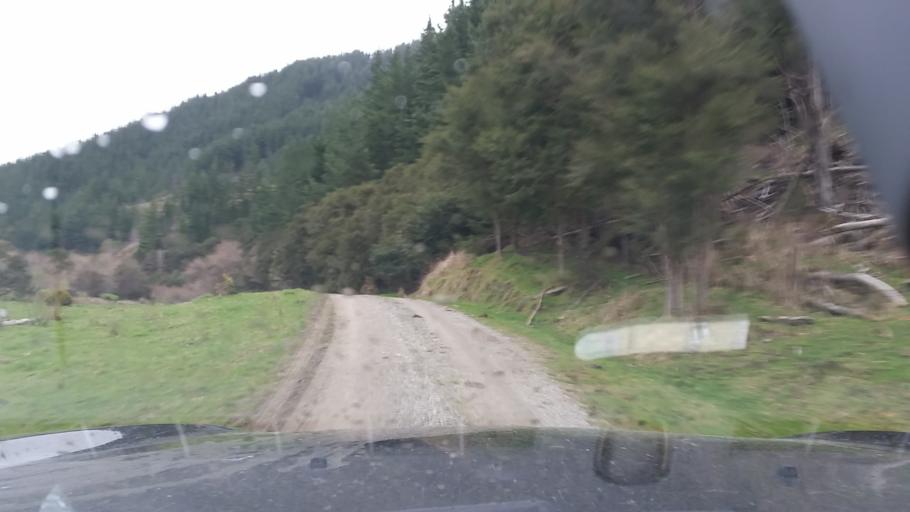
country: NZ
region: Marlborough
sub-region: Marlborough District
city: Blenheim
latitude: -41.3873
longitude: 173.8494
